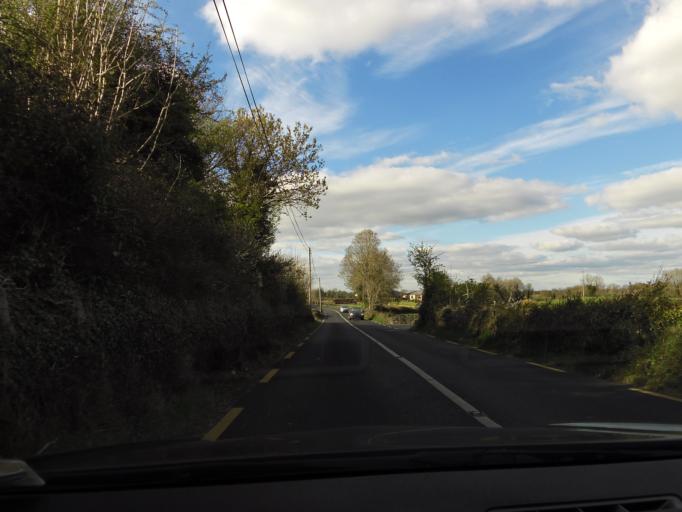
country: IE
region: Connaught
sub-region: County Galway
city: Portumna
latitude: 53.1246
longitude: -8.2437
